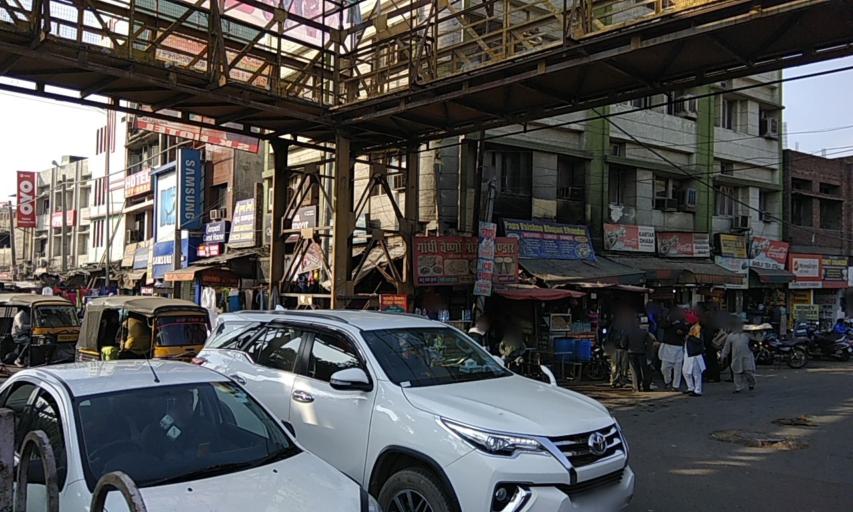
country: IN
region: Punjab
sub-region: Amritsar
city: Amritsar
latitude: 31.6345
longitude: 74.8677
